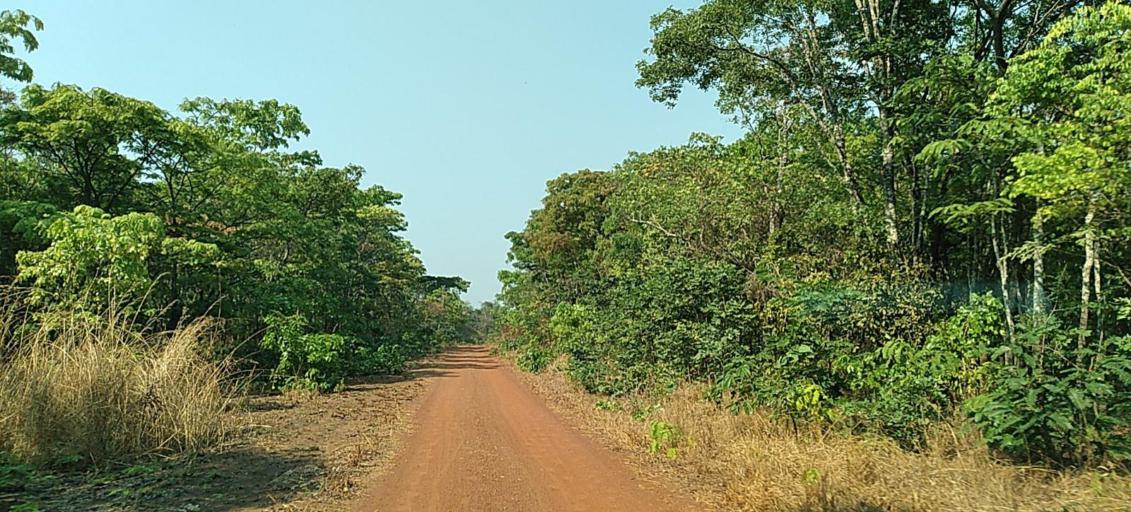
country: ZM
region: Copperbelt
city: Chingola
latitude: -12.8743
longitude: 27.4488
